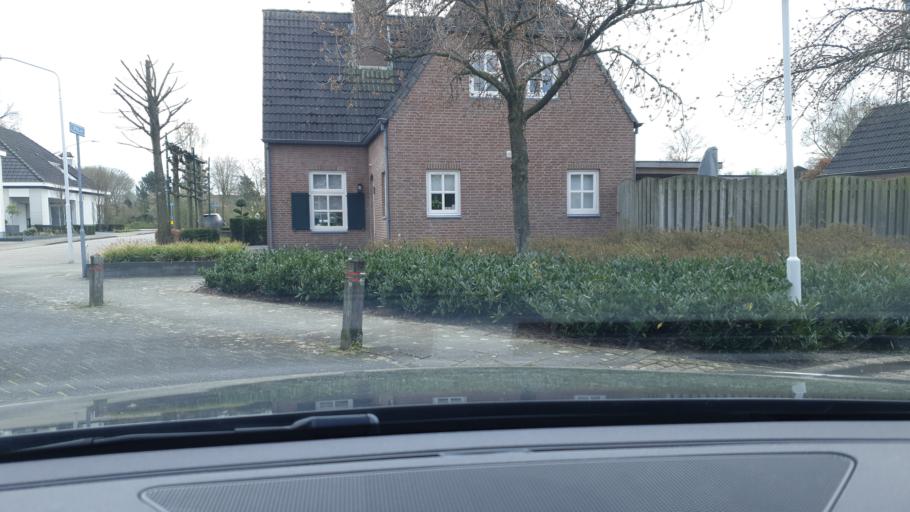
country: NL
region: North Brabant
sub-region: Gemeente Best
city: Best
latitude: 51.4991
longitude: 5.3847
